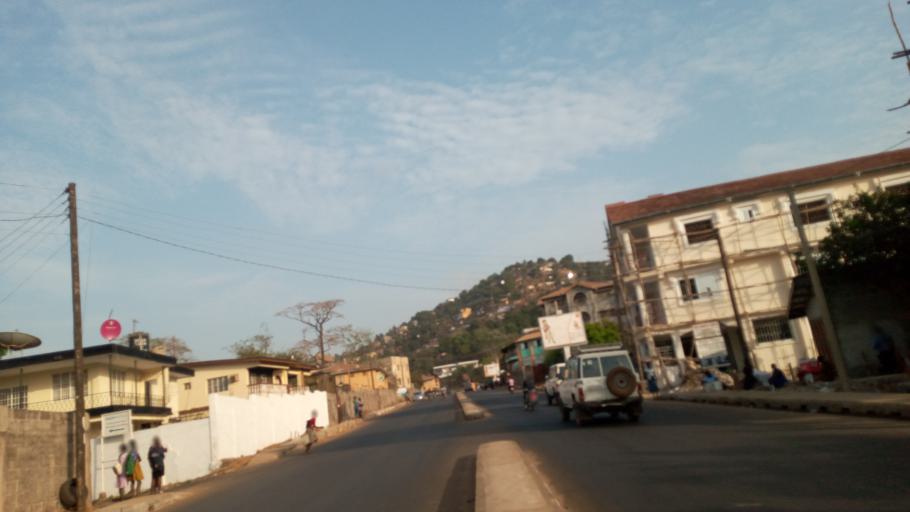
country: SL
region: Western Area
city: Freetown
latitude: 8.4719
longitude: -13.2477
